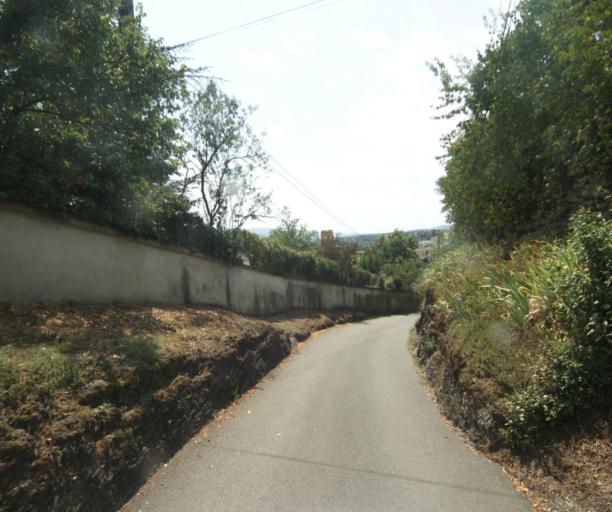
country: FR
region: Rhone-Alpes
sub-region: Departement du Rhone
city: Saint-Germain-Nuelles
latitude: 45.8383
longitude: 4.6200
